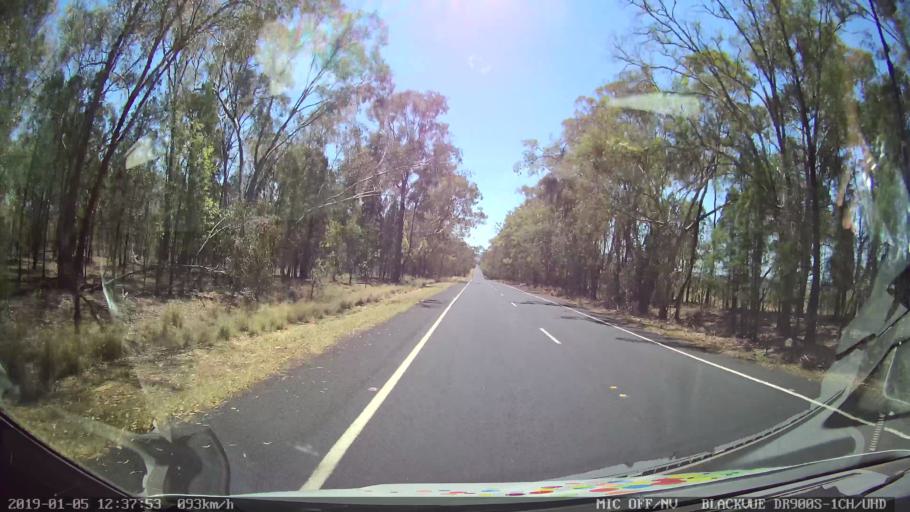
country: AU
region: New South Wales
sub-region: Warrumbungle Shire
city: Coonabarabran
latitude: -31.2003
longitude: 149.4609
